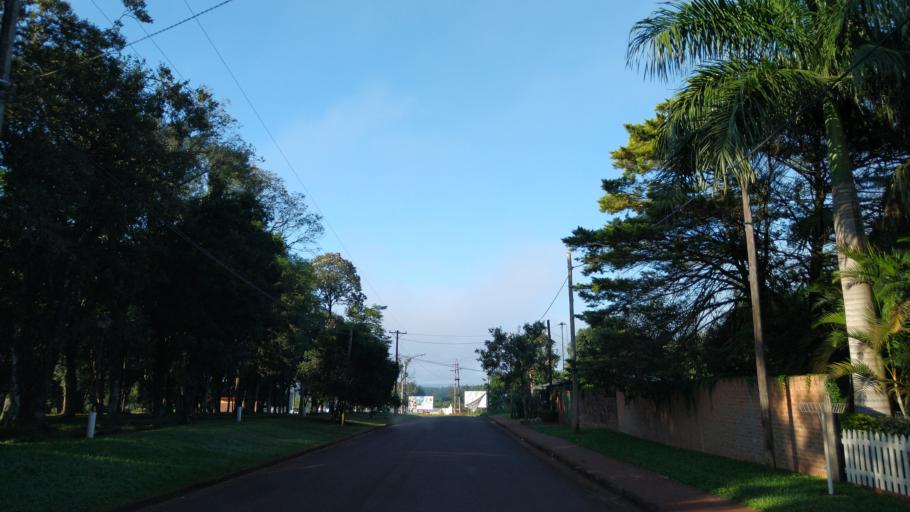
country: AR
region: Misiones
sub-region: Departamento de Montecarlo
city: Montecarlo
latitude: -26.5681
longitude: -54.7734
